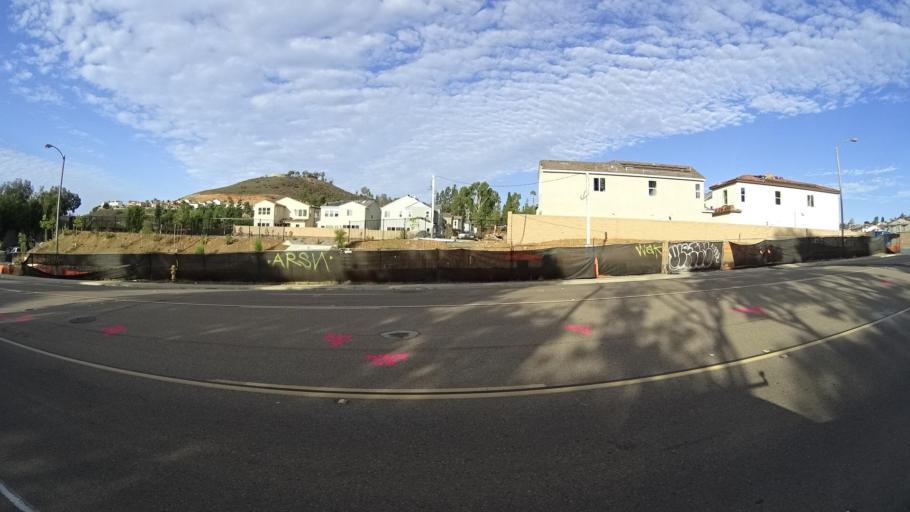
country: US
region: California
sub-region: San Diego County
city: Spring Valley
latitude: 32.7295
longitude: -116.9714
